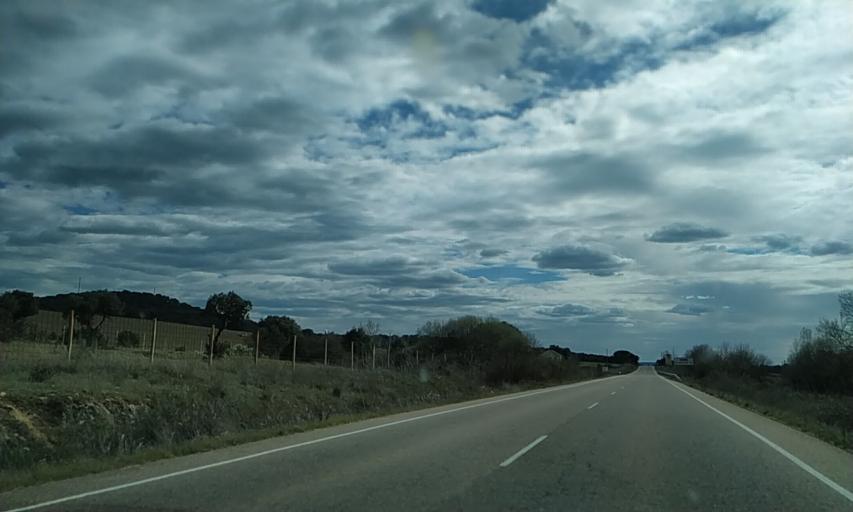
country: ES
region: Castille and Leon
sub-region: Provincia de Salamanca
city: Ciudad Rodrigo
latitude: 40.5754
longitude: -6.5407
